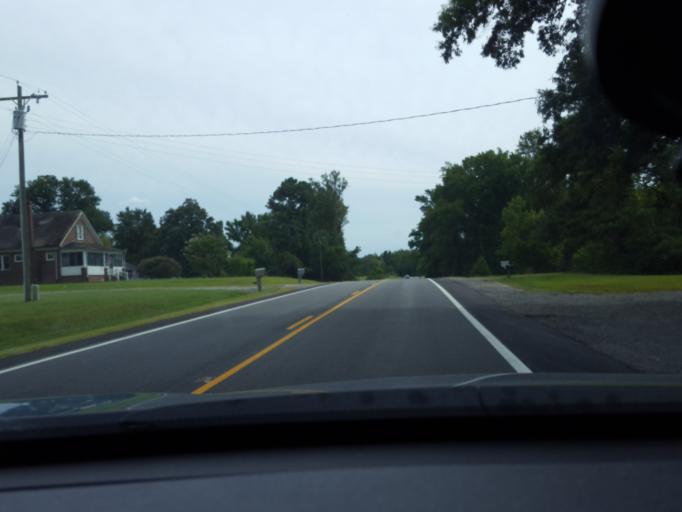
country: US
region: Virginia
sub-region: Hanover County
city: Hanover
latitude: 37.8169
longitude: -77.3732
